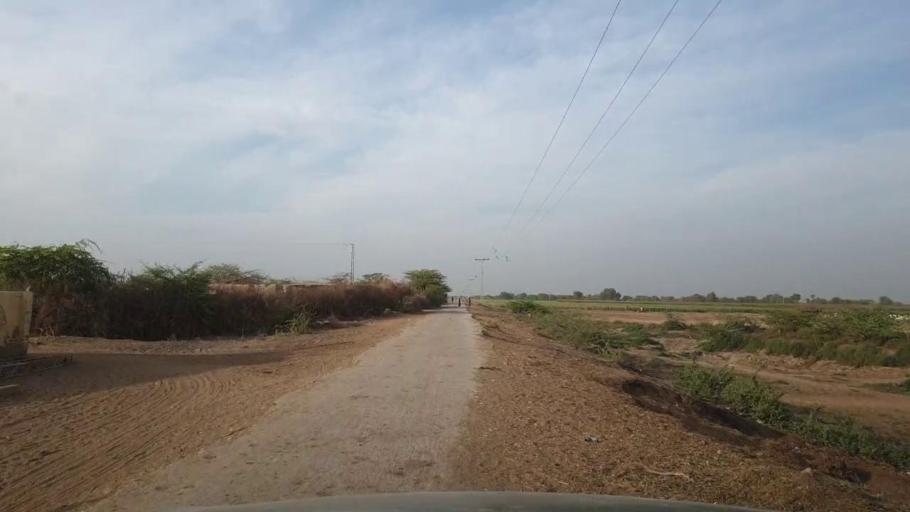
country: PK
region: Sindh
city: Kunri
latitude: 25.1955
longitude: 69.5199
